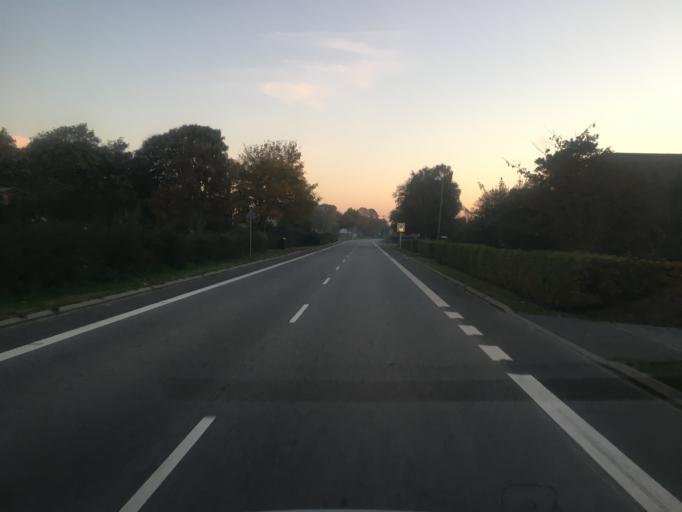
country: DE
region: Schleswig-Holstein
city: Bramstedtlund
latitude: 54.9354
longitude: 9.0758
